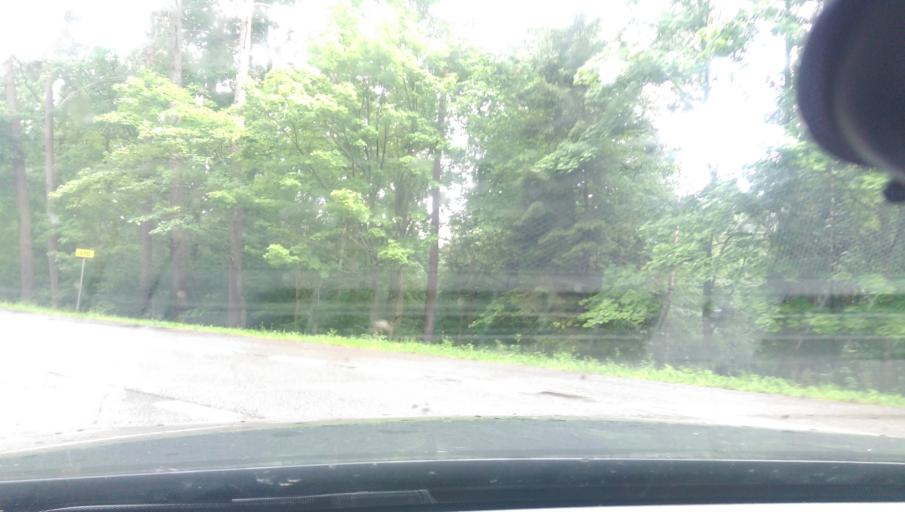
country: PL
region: Warmian-Masurian Voivodeship
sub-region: Powiat mragowski
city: Piecki
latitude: 53.7224
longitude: 21.4160
